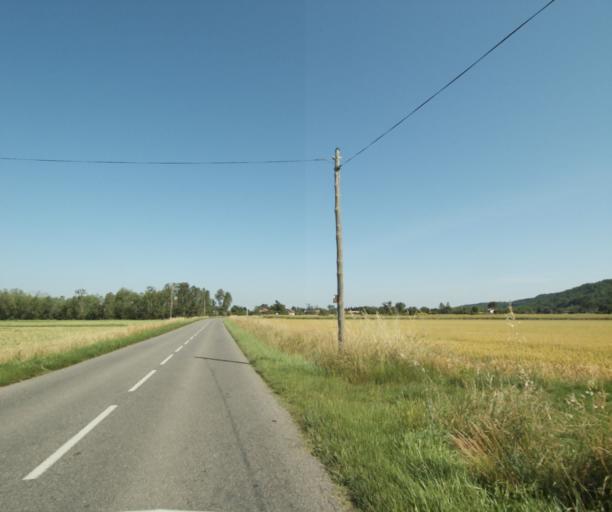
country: FR
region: Midi-Pyrenees
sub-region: Departement du Tarn-et-Garonne
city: Corbarieu
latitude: 43.9631
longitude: 1.3602
